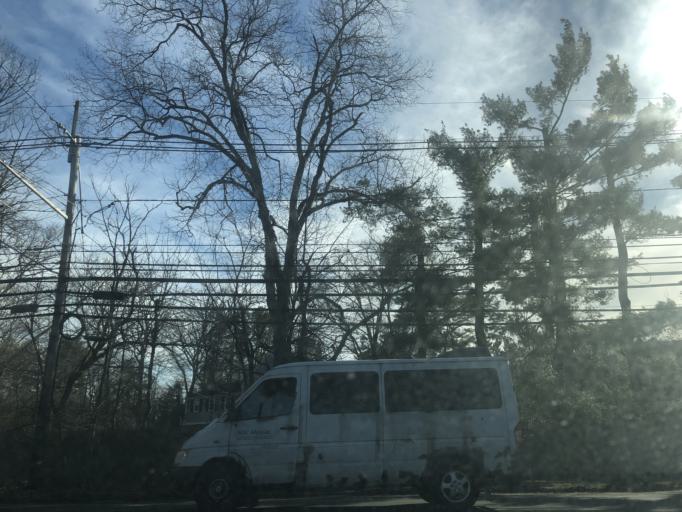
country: US
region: New Jersey
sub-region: Mercer County
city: Princeton
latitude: 40.3590
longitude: -74.6347
